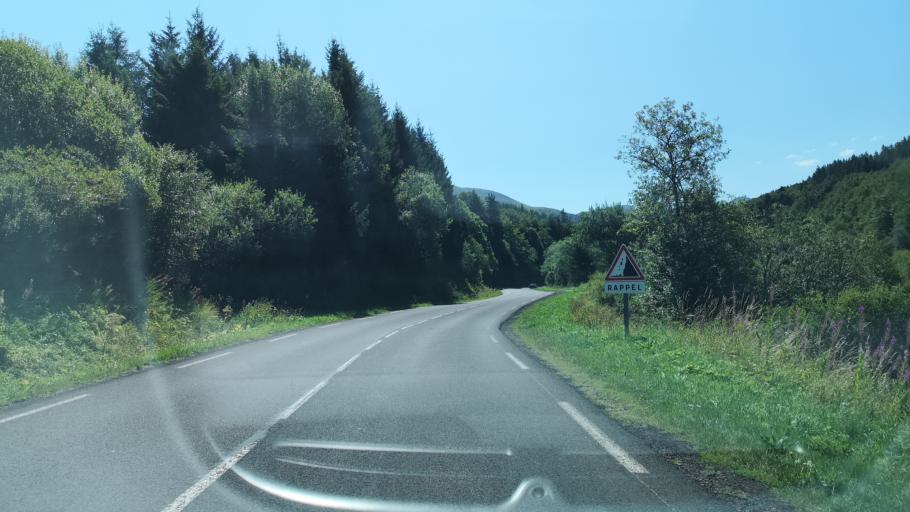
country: FR
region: Auvergne
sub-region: Departement du Puy-de-Dome
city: Mont-Dore
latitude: 45.6104
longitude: 2.8249
